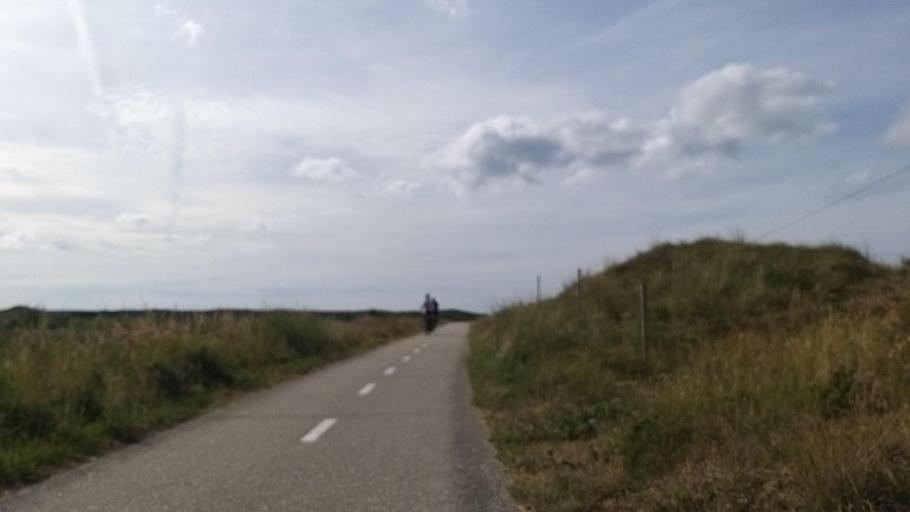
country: NL
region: North Holland
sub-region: Gemeente Texel
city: Den Burg
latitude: 53.1588
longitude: 4.8290
